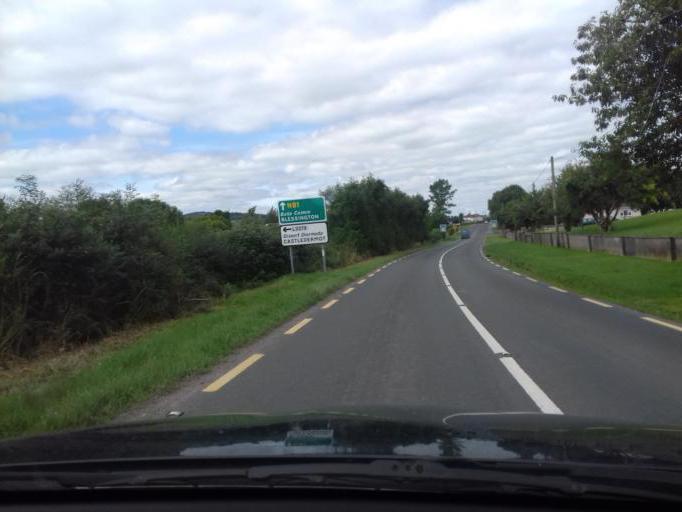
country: IE
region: Leinster
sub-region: Wicklow
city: Baltinglass
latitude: 52.9293
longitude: -6.7101
